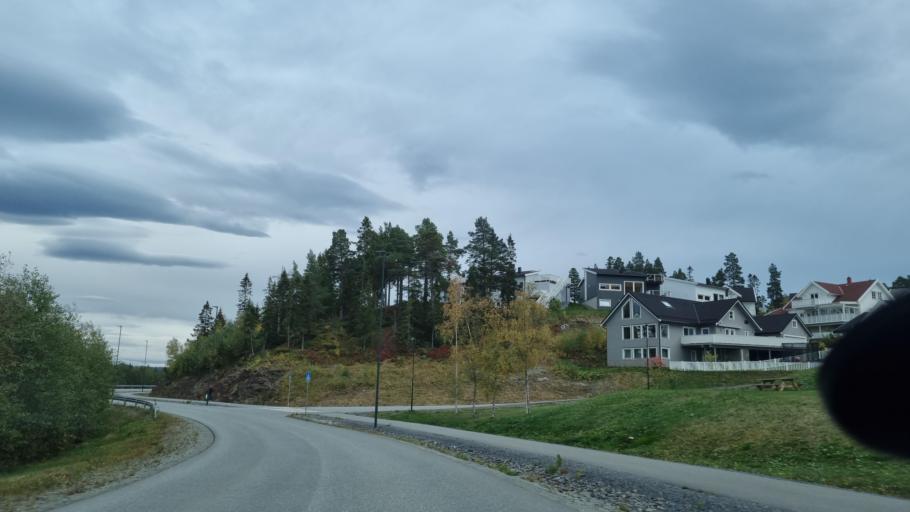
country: NO
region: Sor-Trondelag
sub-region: Malvik
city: Hommelvik
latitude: 63.4259
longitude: 10.7589
